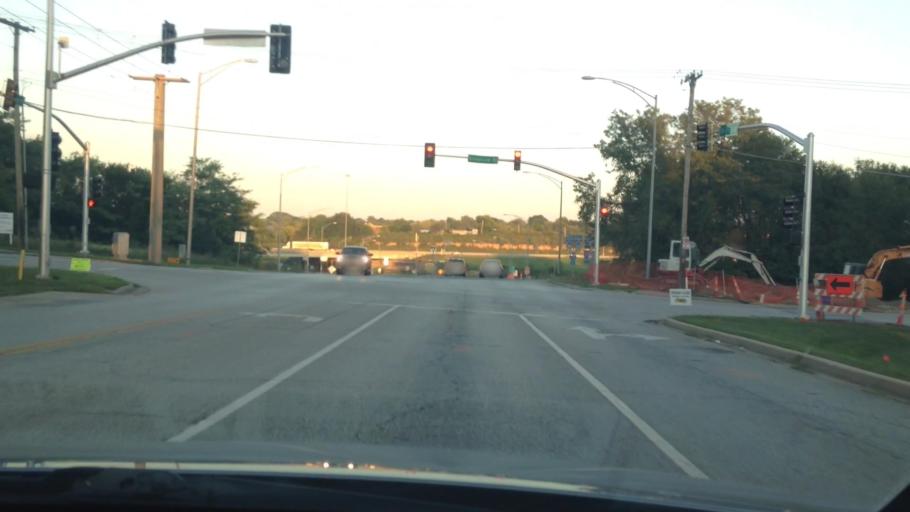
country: US
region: Missouri
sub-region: Jackson County
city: Grandview
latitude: 38.9238
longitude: -94.5329
